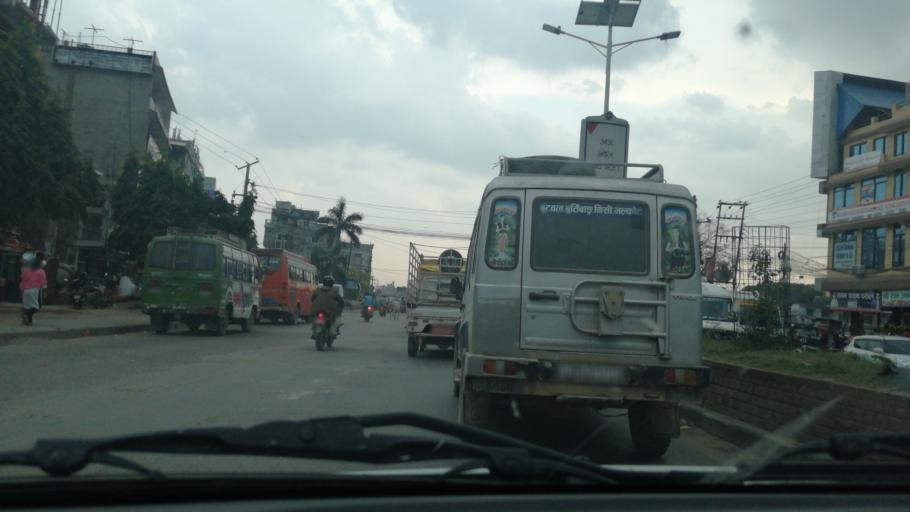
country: NP
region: Western Region
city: Butwal
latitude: 27.6991
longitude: 83.4656
